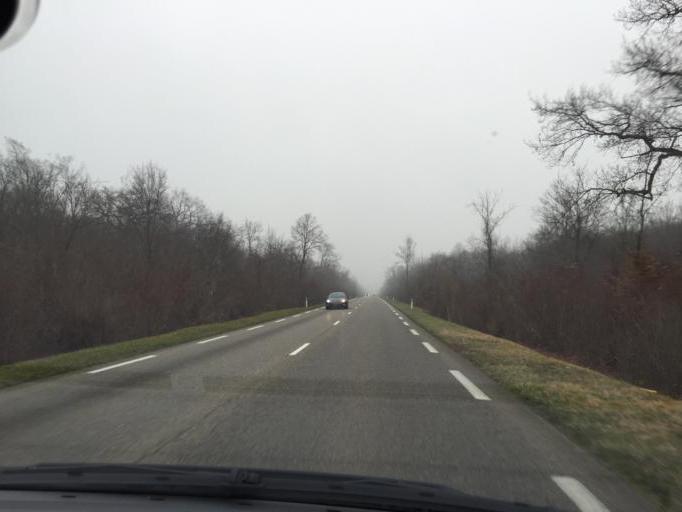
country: FR
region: Alsace
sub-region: Departement du Haut-Rhin
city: Widensolen
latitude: 48.0491
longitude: 7.4577
